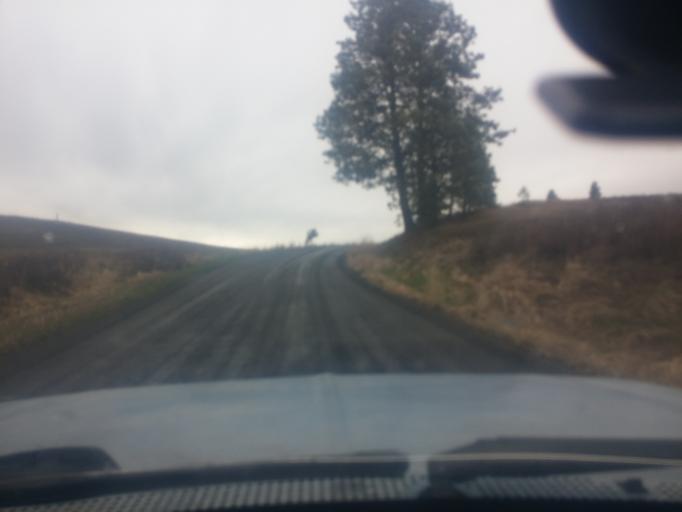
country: US
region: Idaho
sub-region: Latah County
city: Moscow
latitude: 46.9299
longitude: -116.8702
